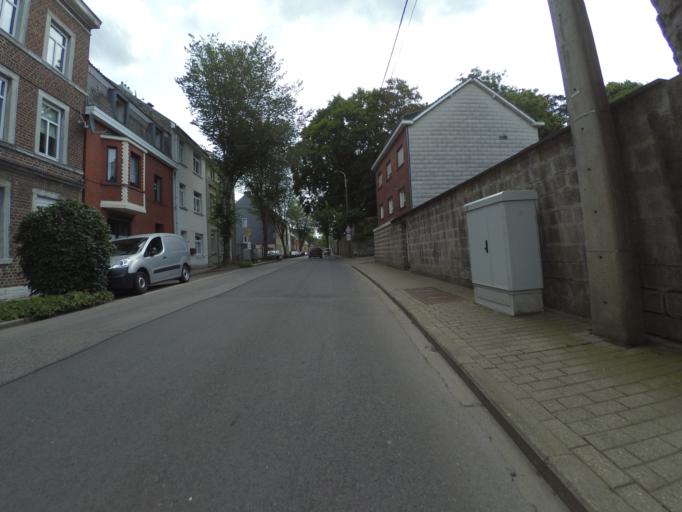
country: BE
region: Wallonia
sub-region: Province de Liege
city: Eupen
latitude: 50.6208
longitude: 6.0439
